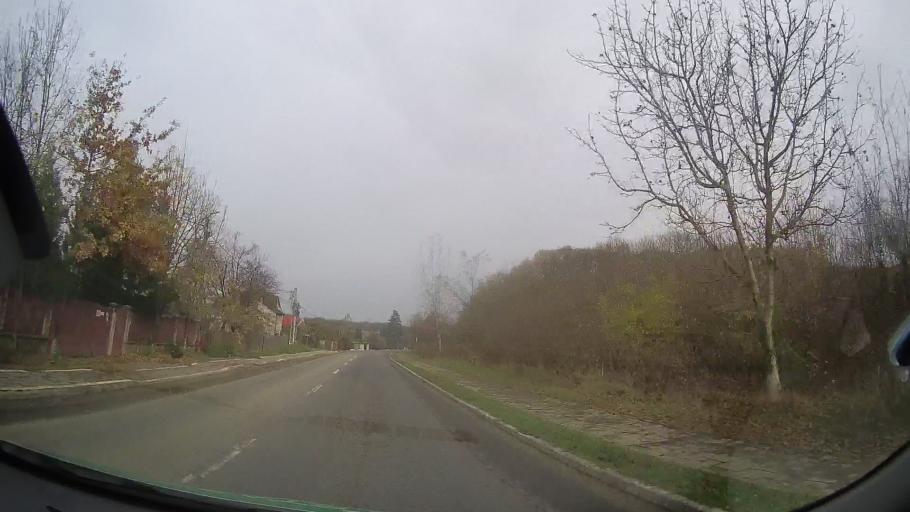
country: RO
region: Ilfov
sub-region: Comuna Snagov
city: Snagov
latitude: 44.7107
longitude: 26.1865
